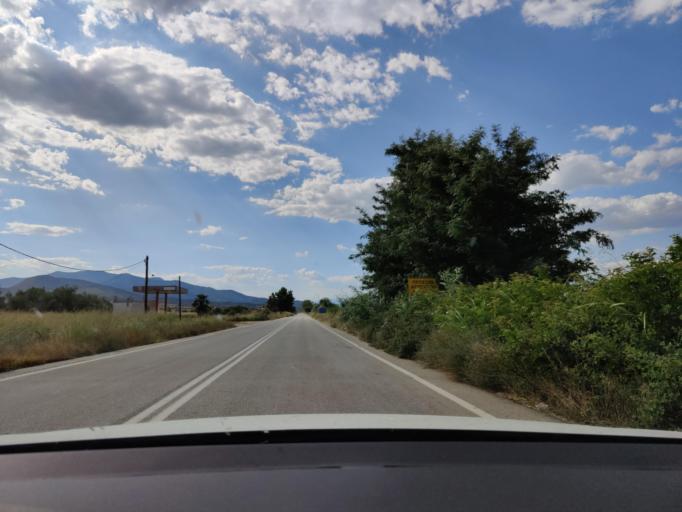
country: GR
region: Central Macedonia
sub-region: Nomos Serron
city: Strymoniko
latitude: 41.0888
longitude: 23.2829
